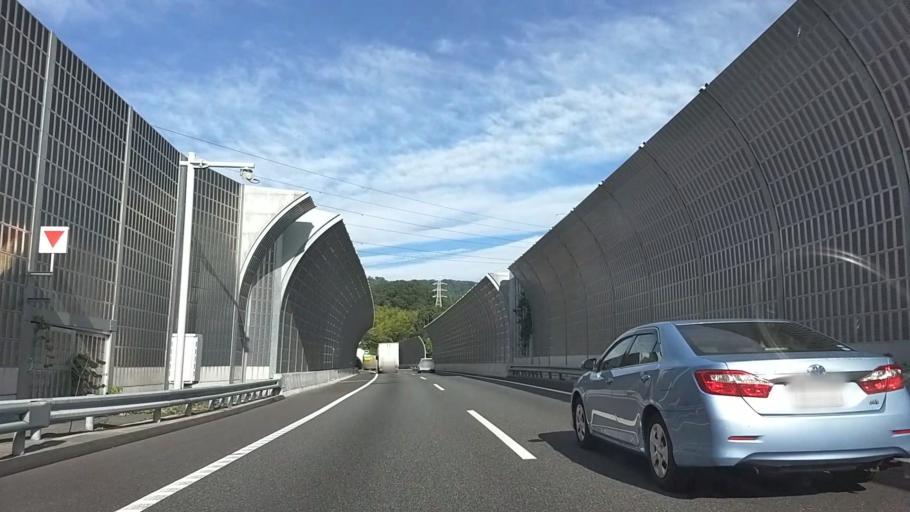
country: JP
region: Tokyo
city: Hachioji
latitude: 35.5950
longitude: 139.2821
